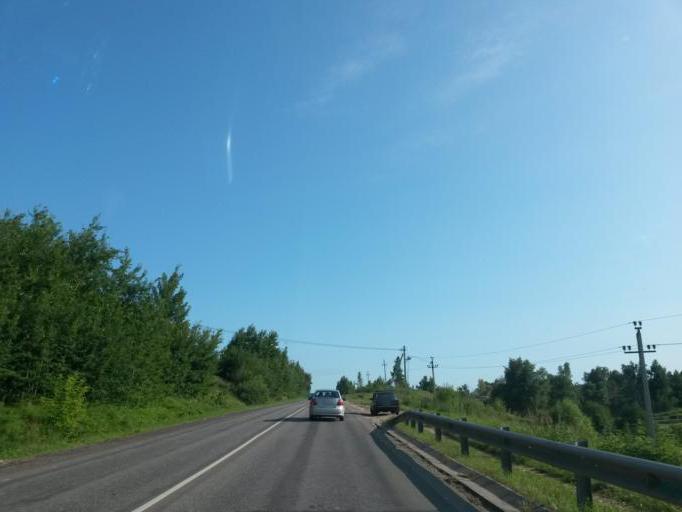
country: RU
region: Moskovskaya
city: Gorki-Leninskiye
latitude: 55.4933
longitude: 37.7804
